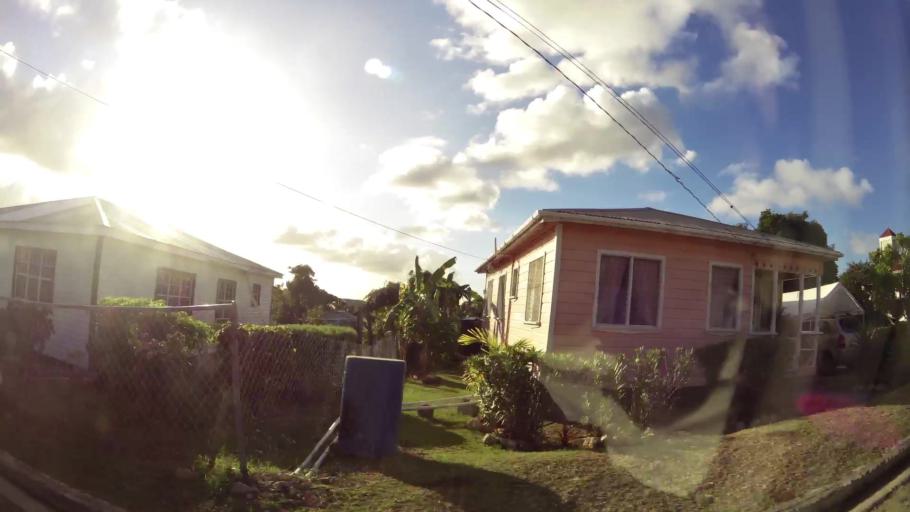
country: AG
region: Saint George
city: Piggotts
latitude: 17.1230
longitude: -61.8022
